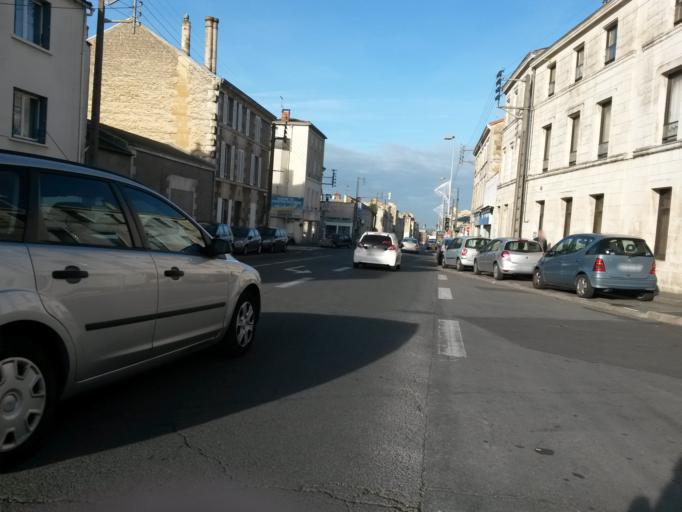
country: FR
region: Poitou-Charentes
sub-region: Departement des Deux-Sevres
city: Niort
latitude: 46.3196
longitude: -0.4502
